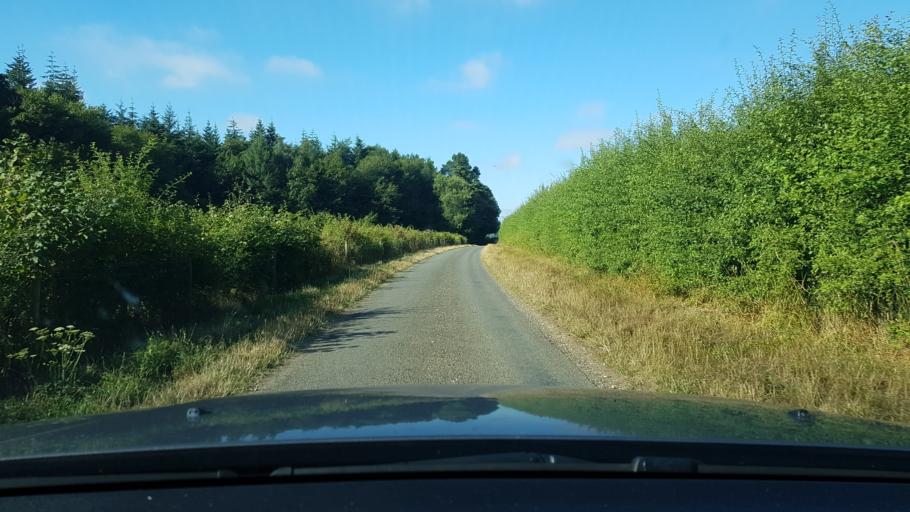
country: GB
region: England
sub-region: Wiltshire
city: Chilton Foliat
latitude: 51.4531
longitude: -1.5668
